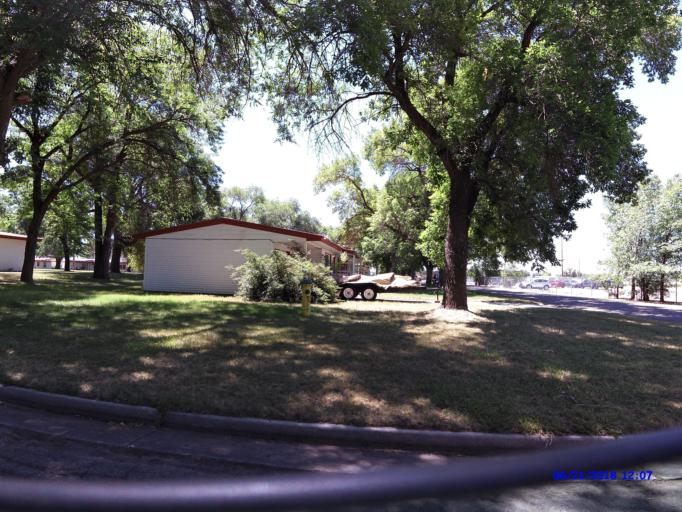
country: US
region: Utah
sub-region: Weber County
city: Harrisville
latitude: 41.2853
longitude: -112.0072
